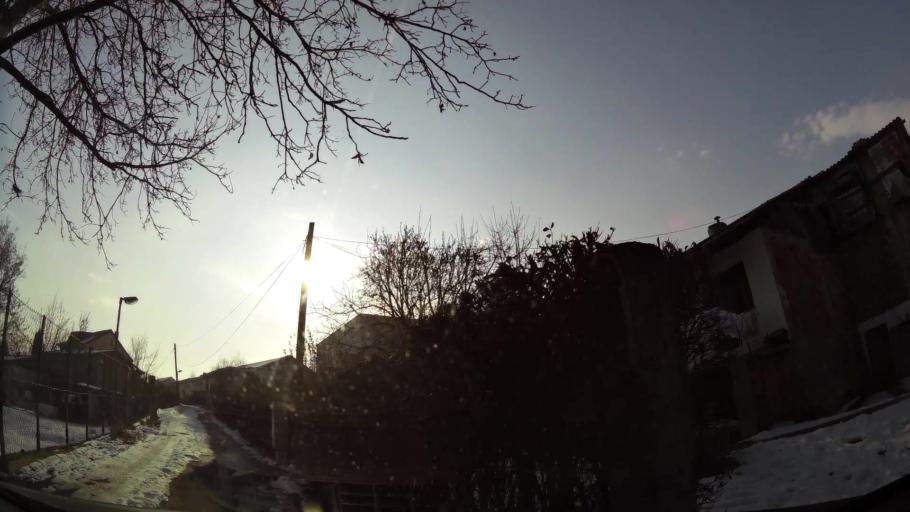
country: MK
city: Creshevo
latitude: 42.0167
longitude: 21.5047
